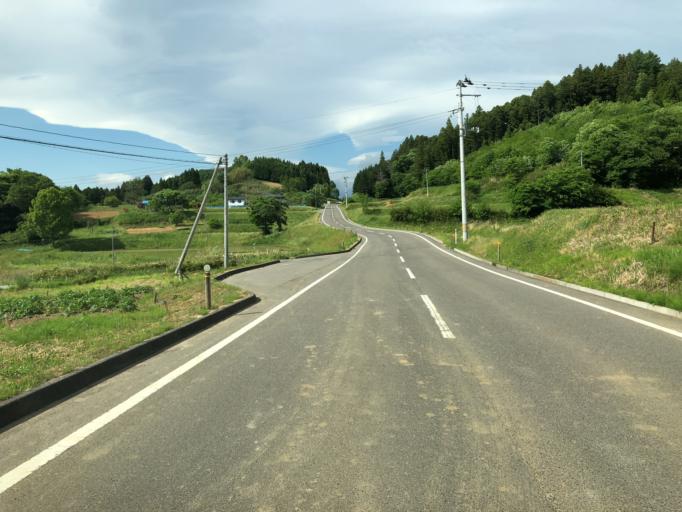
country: JP
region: Fukushima
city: Nihommatsu
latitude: 37.5961
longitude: 140.5172
